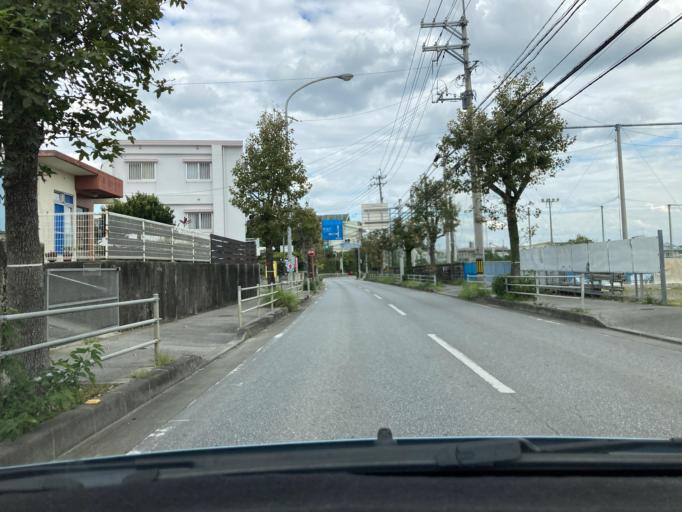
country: JP
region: Okinawa
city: Gushikawa
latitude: 26.3493
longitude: 127.8473
